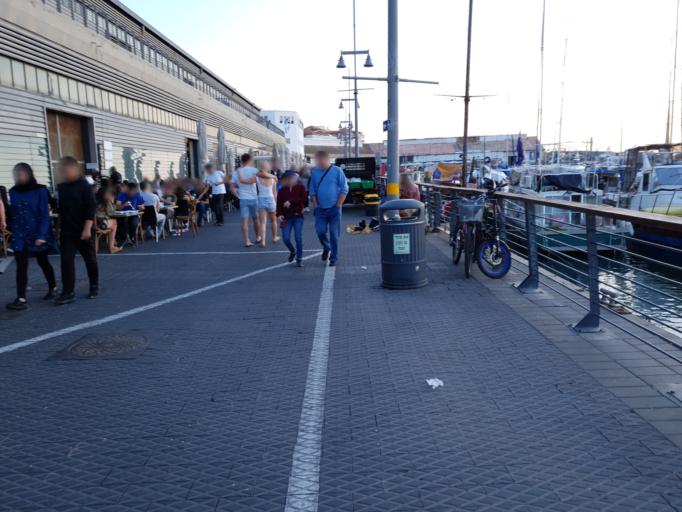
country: IL
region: Tel Aviv
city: Yafo
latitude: 32.0534
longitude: 34.7498
